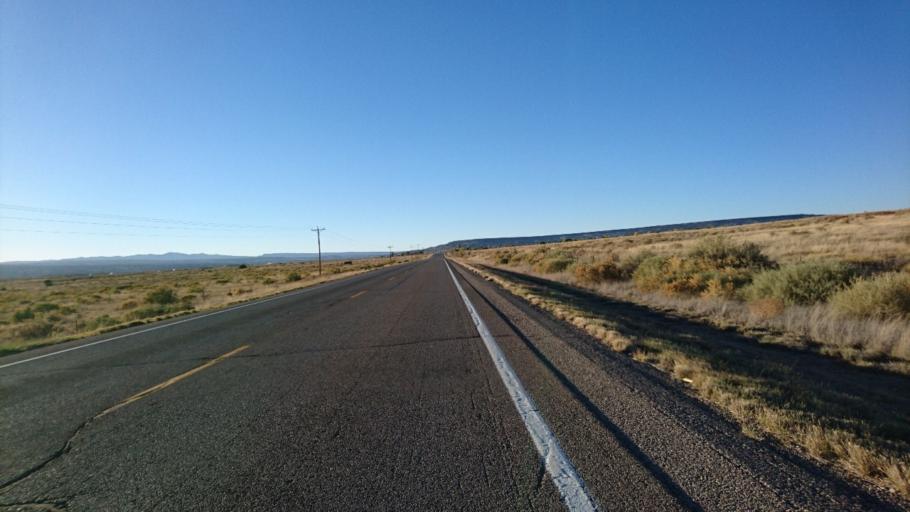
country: US
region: New Mexico
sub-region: Cibola County
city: Grants
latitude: 35.1207
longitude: -107.7948
